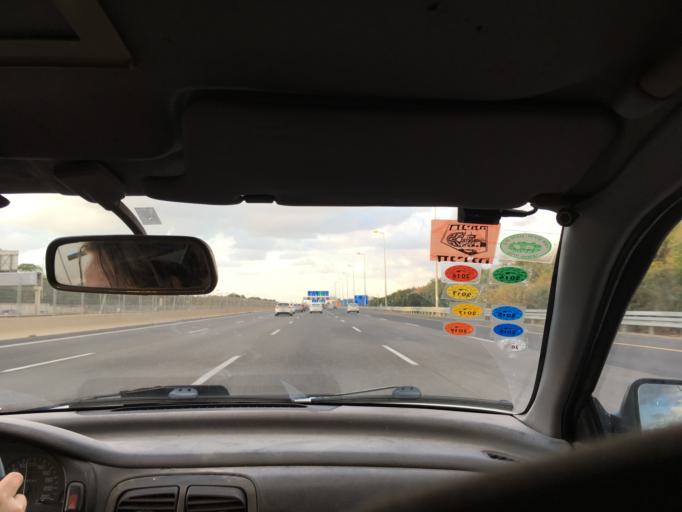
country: IL
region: Tel Aviv
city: Ramat HaSharon
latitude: 32.1248
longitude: 34.8106
